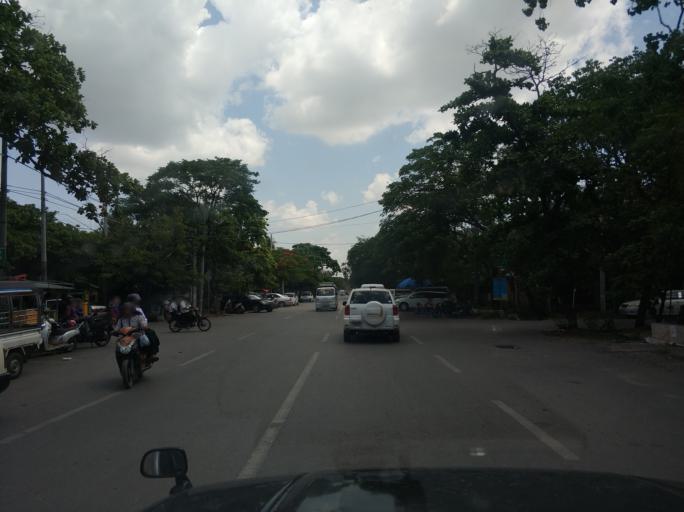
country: MM
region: Mandalay
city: Mandalay
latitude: 21.9788
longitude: 96.1036
